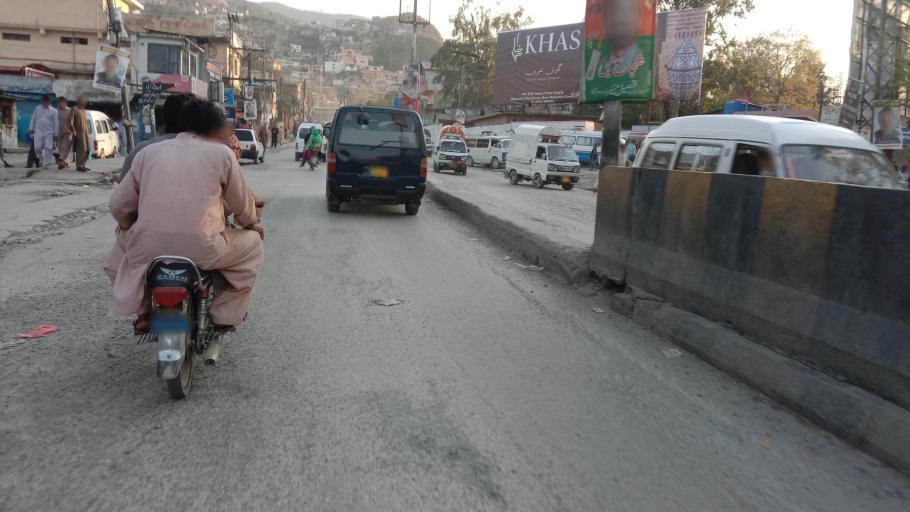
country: PK
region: Khyber Pakhtunkhwa
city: Abbottabad
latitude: 34.1443
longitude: 73.2148
